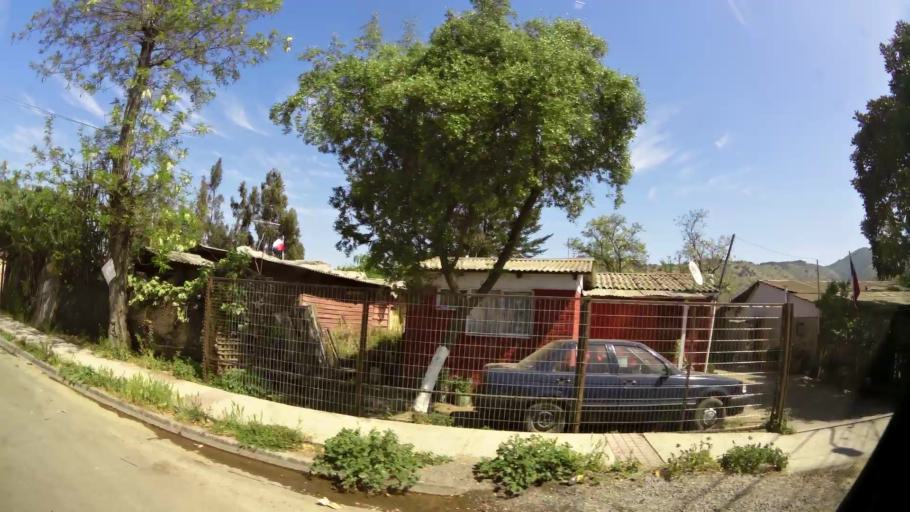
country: CL
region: Santiago Metropolitan
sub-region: Provincia de Talagante
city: Talagante
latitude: -33.6543
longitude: -70.9308
